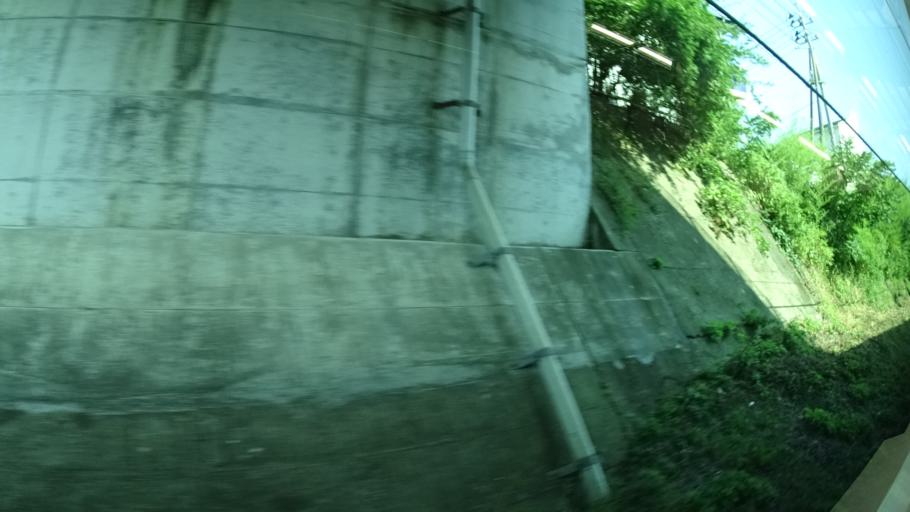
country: JP
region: Miyagi
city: Shiogama
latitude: 38.3119
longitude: 141.0098
